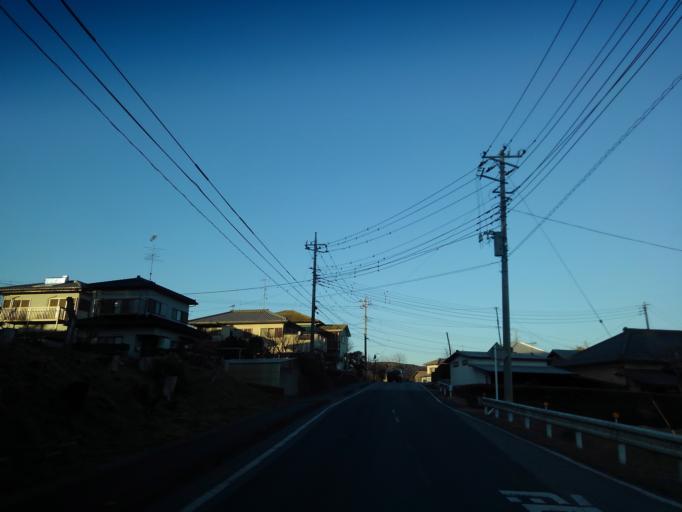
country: JP
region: Chiba
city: Kimitsu
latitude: 35.3003
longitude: 139.9831
